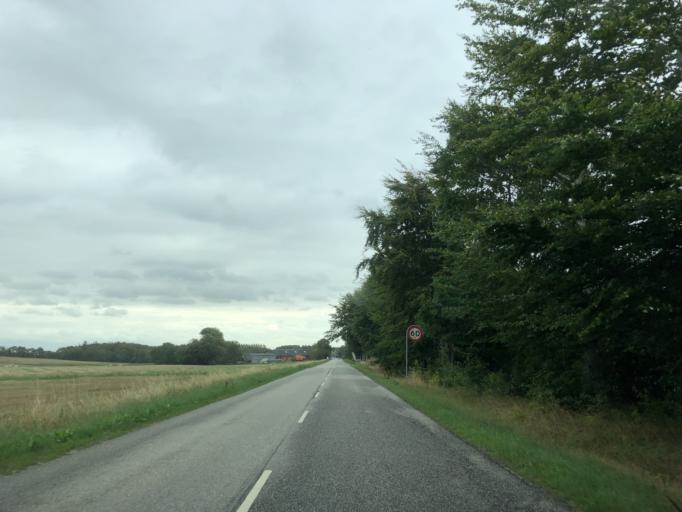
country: DK
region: Central Jutland
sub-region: Herning Kommune
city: Snejbjerg
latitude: 56.1764
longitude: 8.8389
